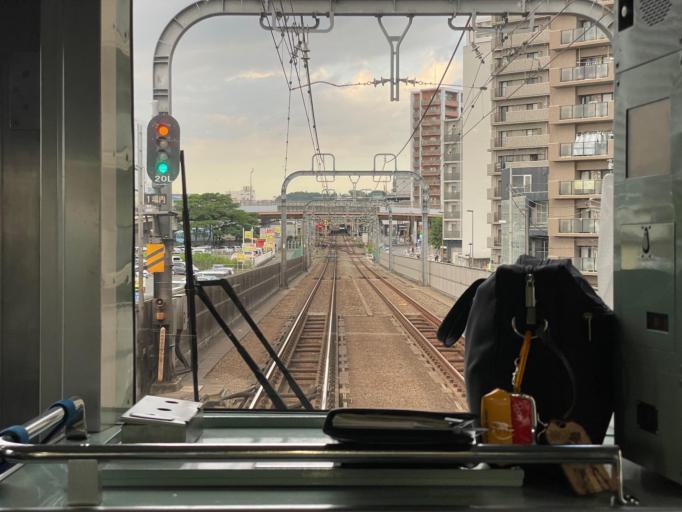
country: JP
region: Kanagawa
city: Atsugi
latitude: 35.4497
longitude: 139.3870
